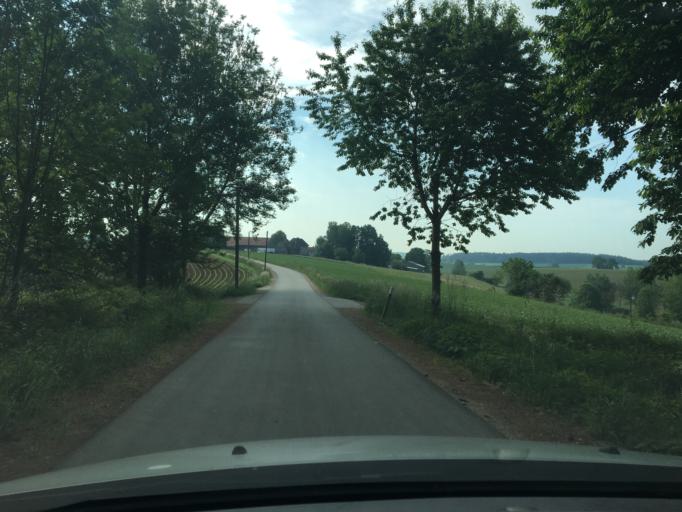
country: DE
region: Bavaria
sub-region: Upper Bavaria
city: Egglkofen
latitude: 48.4082
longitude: 12.4286
